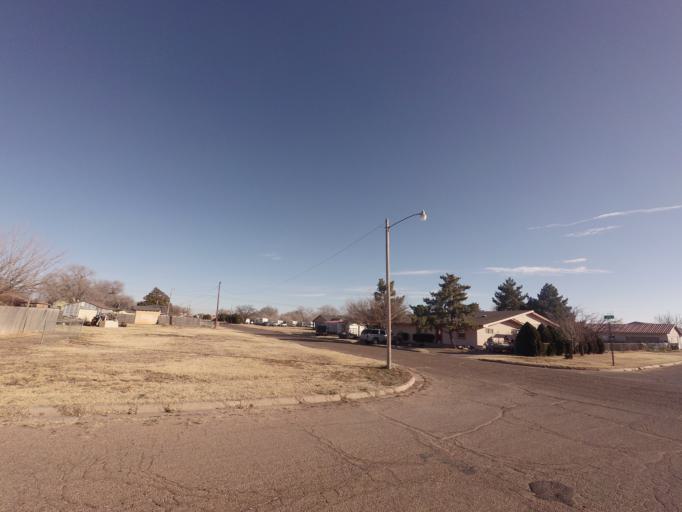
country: US
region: New Mexico
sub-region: Curry County
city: Clovis
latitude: 34.4020
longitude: -103.1852
